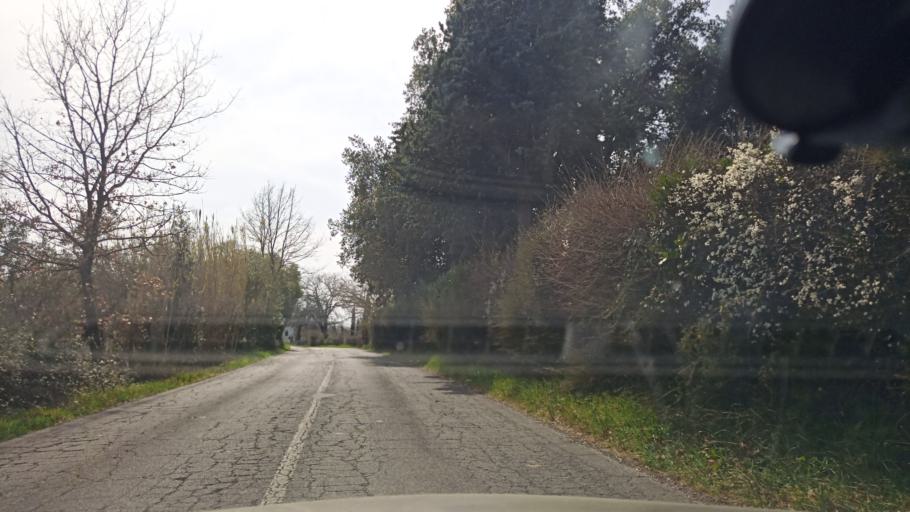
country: IT
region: Latium
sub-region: Provincia di Rieti
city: Torri in Sabina
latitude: 42.3583
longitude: 12.6513
